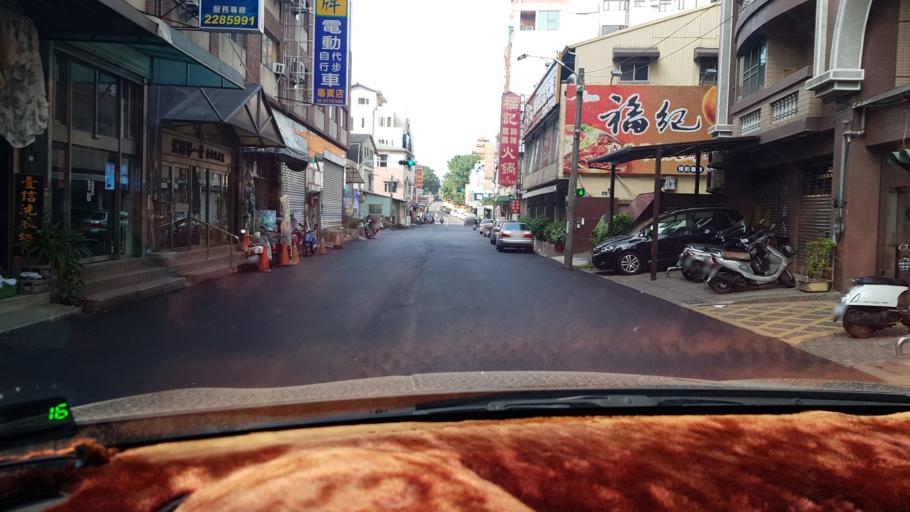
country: TW
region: Taiwan
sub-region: Chiayi
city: Jiayi Shi
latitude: 23.4842
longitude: 120.4646
